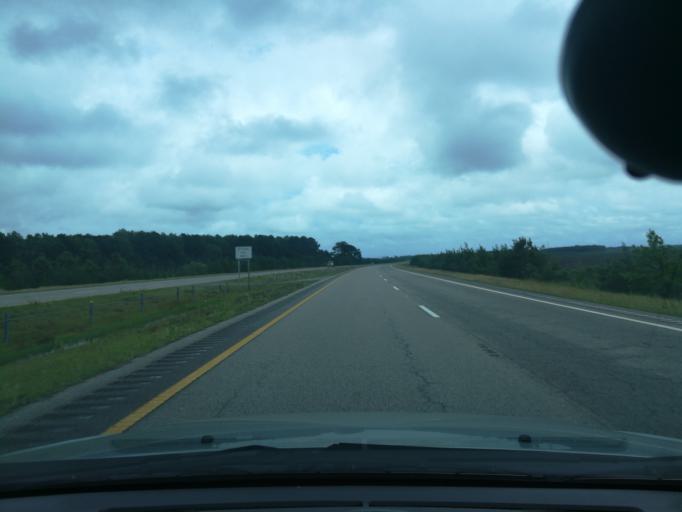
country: US
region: North Carolina
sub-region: Chowan County
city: Edenton
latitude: 35.9038
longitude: -76.4948
